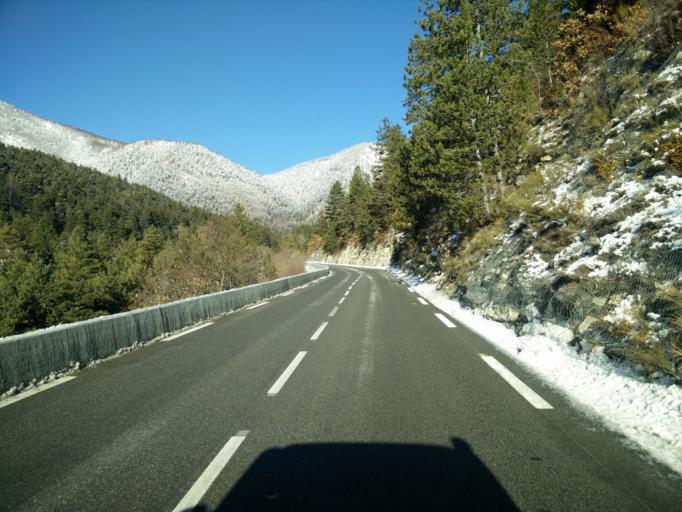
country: FR
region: Provence-Alpes-Cote d'Azur
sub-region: Departement des Alpes-de-Haute-Provence
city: Annot
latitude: 43.9347
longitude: 6.6377
